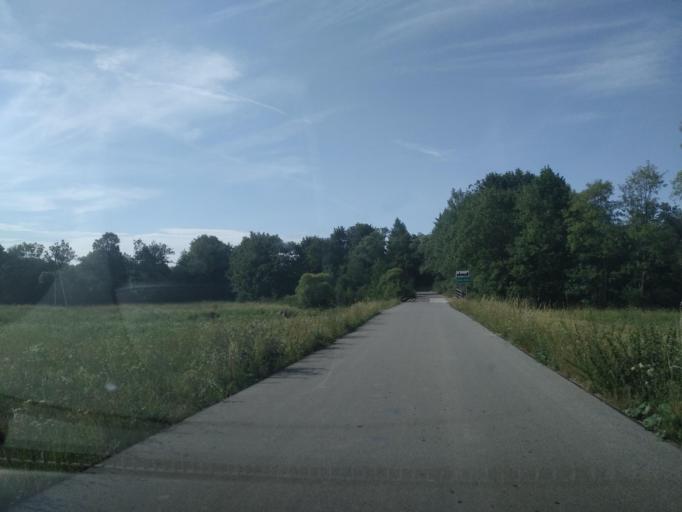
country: PL
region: Subcarpathian Voivodeship
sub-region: Powiat krosnienski
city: Jasliska
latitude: 49.4173
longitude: 21.8571
